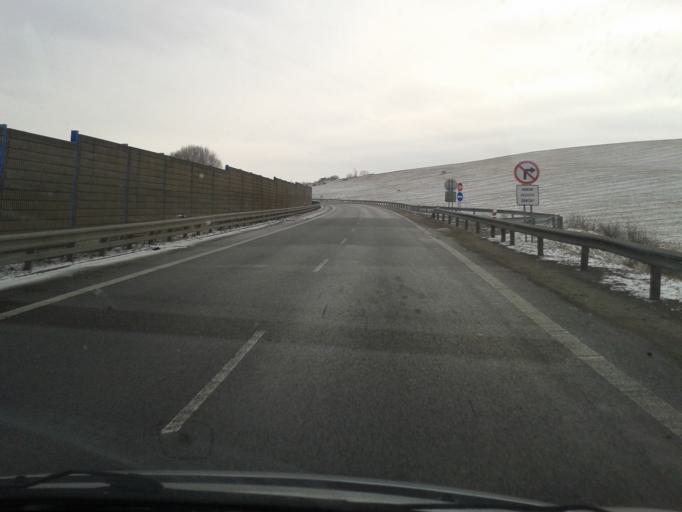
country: SK
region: Zilinsky
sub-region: Okres Zilina
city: Trstena
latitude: 49.3521
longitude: 19.6035
